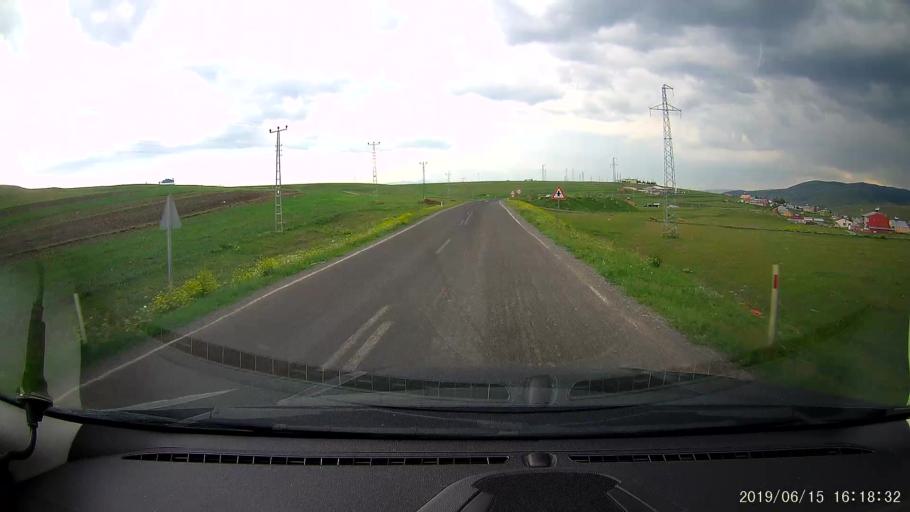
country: TR
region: Ardahan
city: Hanak
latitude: 41.2386
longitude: 42.8516
